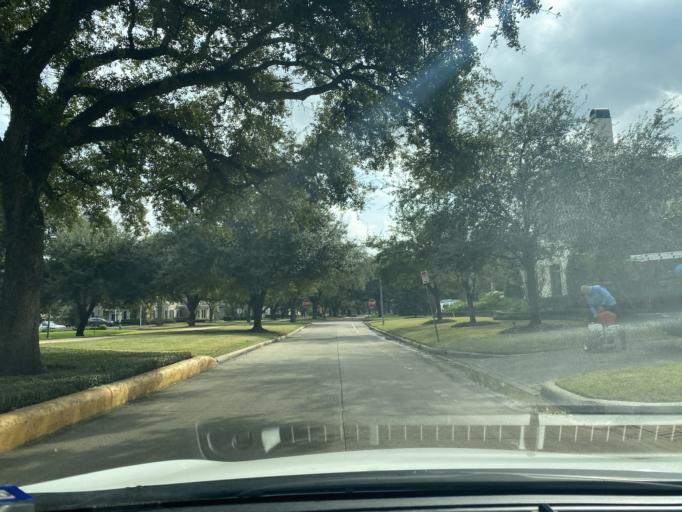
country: US
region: Texas
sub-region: Harris County
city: Hunters Creek Village
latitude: 29.7545
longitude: -95.4705
